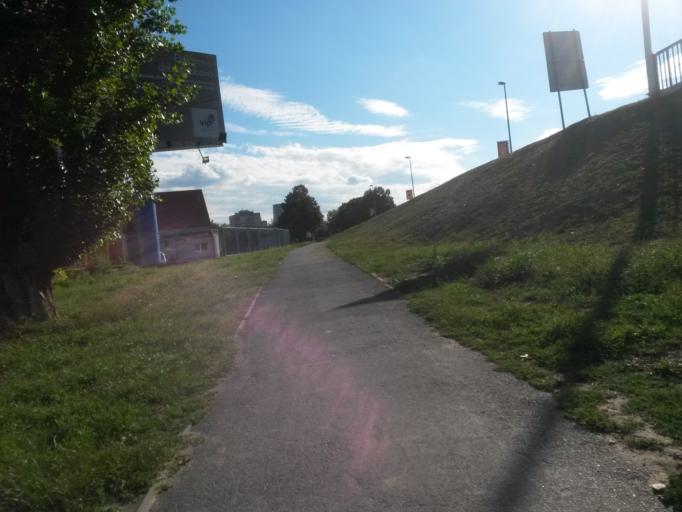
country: HR
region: Osjecko-Baranjska
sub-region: Grad Osijek
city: Osijek
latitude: 45.5609
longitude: 18.7004
